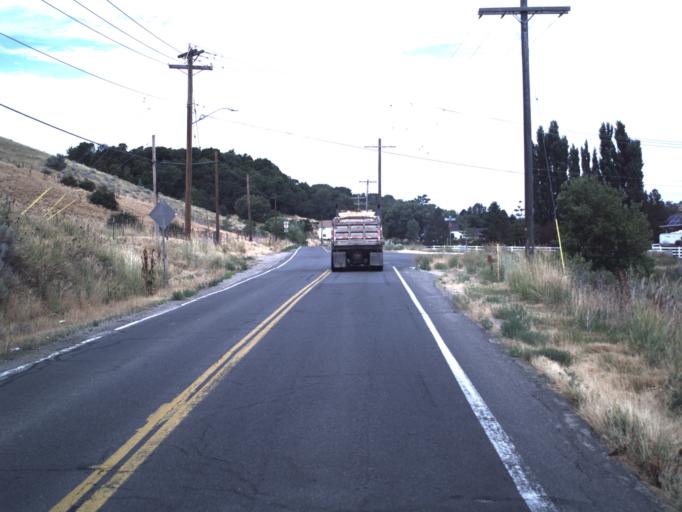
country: US
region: Utah
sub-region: Davis County
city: Hill Air Force Bace
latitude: 41.1394
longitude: -111.9689
